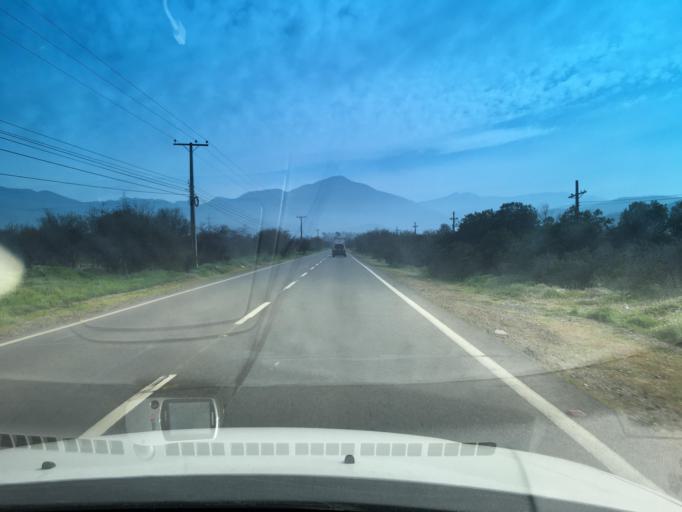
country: CL
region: Santiago Metropolitan
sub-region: Provincia de Chacabuco
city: Lampa
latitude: -33.1301
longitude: -70.9213
